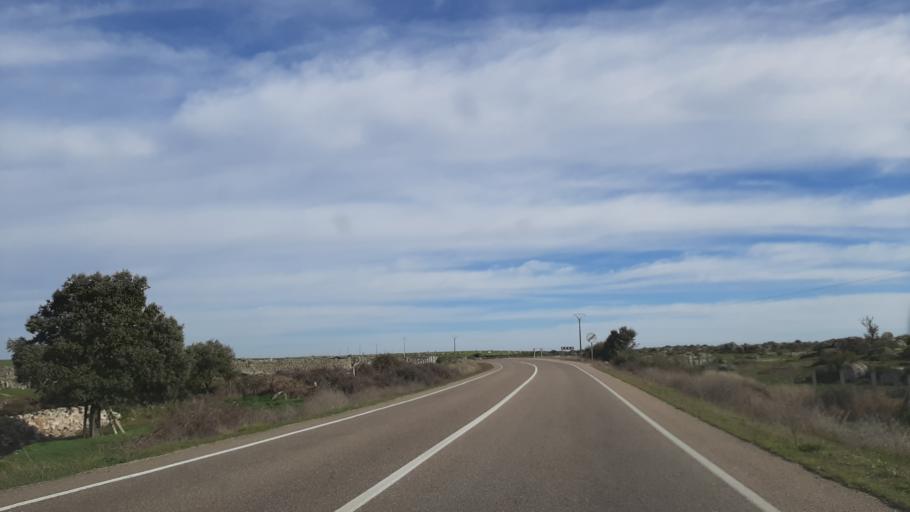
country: ES
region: Castille and Leon
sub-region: Provincia de Salamanca
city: Ledesma
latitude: 41.0911
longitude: -5.9893
